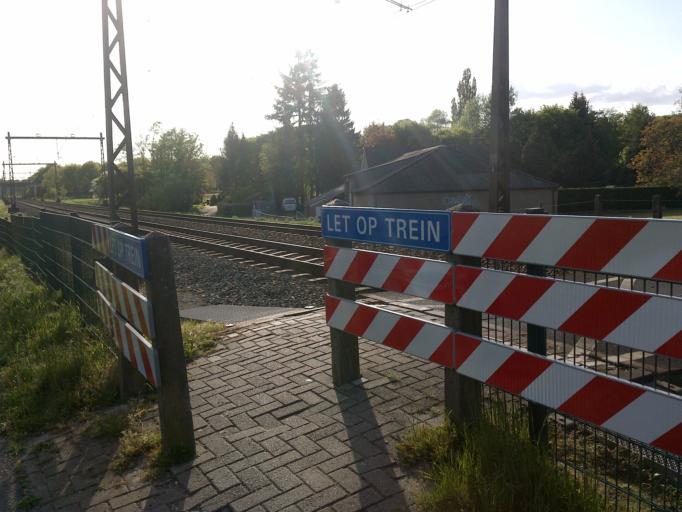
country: NL
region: Gelderland
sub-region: Gemeente Rheden
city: Rheden
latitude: 52.0038
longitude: 6.0078
